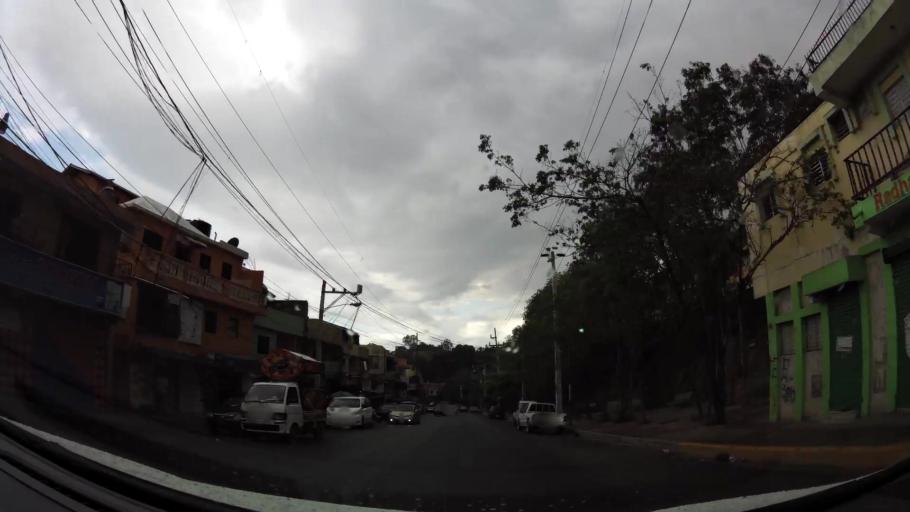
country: DO
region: Nacional
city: La Agustina
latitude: 18.4985
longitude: -69.9298
